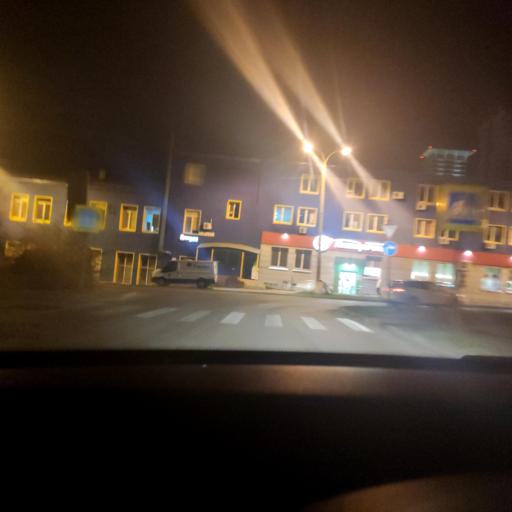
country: RU
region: Samara
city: Samara
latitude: 53.2017
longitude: 50.1504
